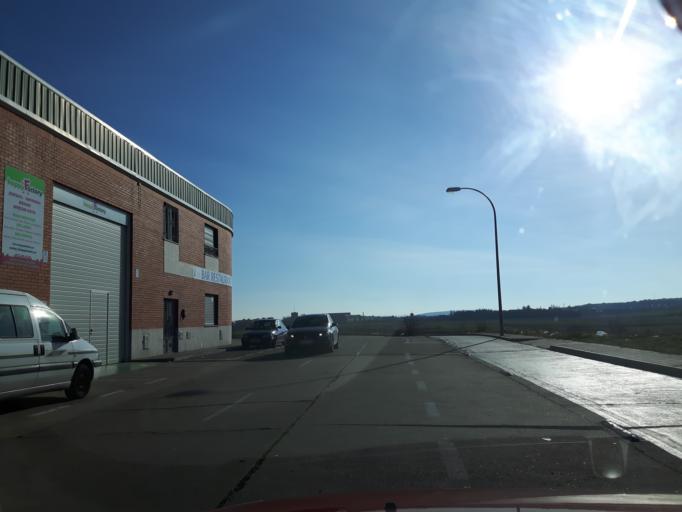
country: ES
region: Castille and Leon
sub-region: Provincia de Salamanca
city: Villares de la Reina
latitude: 40.9911
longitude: -5.6496
